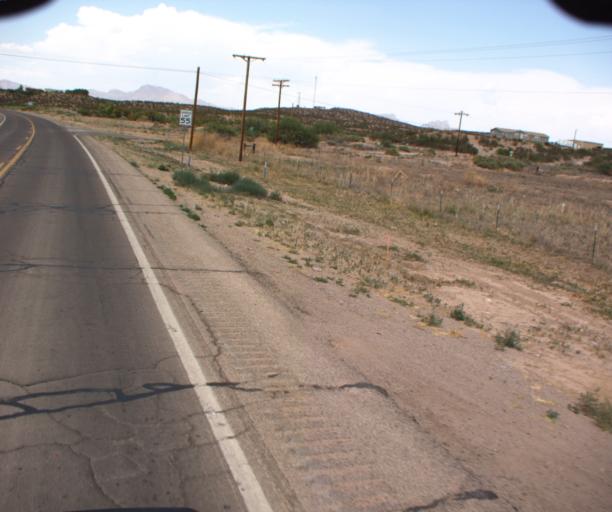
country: US
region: Arizona
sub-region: Greenlee County
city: Clifton
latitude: 32.7295
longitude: -109.0936
